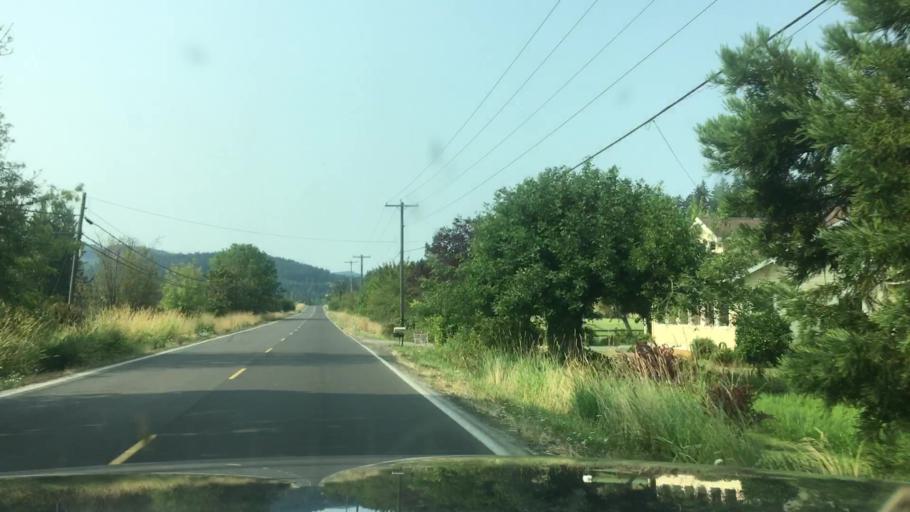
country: US
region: Oregon
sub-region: Lane County
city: Cottage Grove
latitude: 43.7750
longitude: -123.0756
